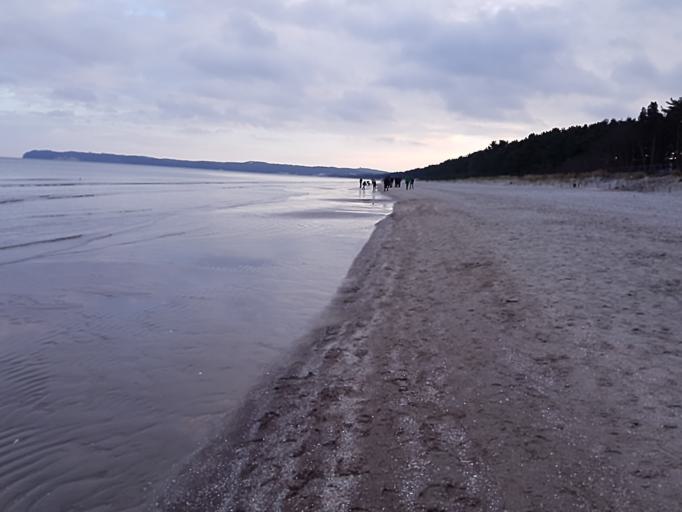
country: DE
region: Mecklenburg-Vorpommern
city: Ostseebad Binz
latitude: 54.4319
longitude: 13.5829
